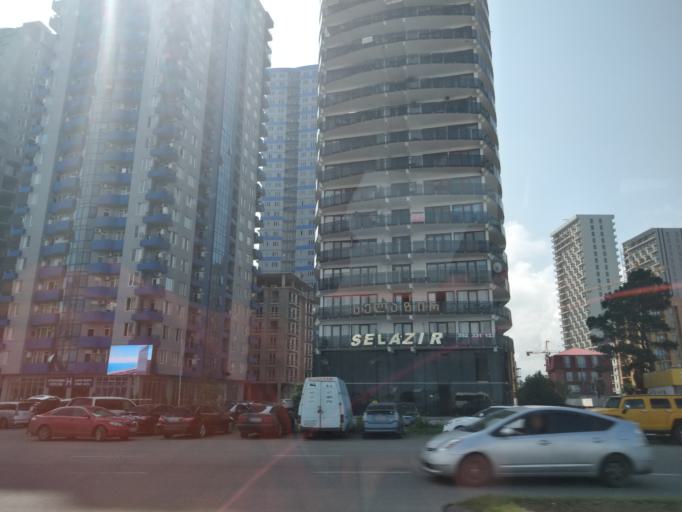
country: GE
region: Ajaria
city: Batumi
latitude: 41.6318
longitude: 41.6025
